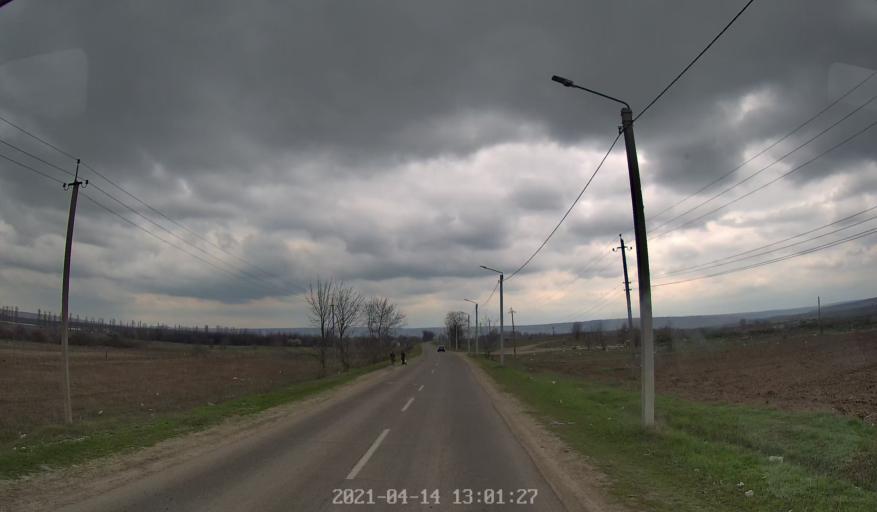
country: MD
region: Chisinau
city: Vadul lui Voda
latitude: 47.1316
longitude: 29.1163
